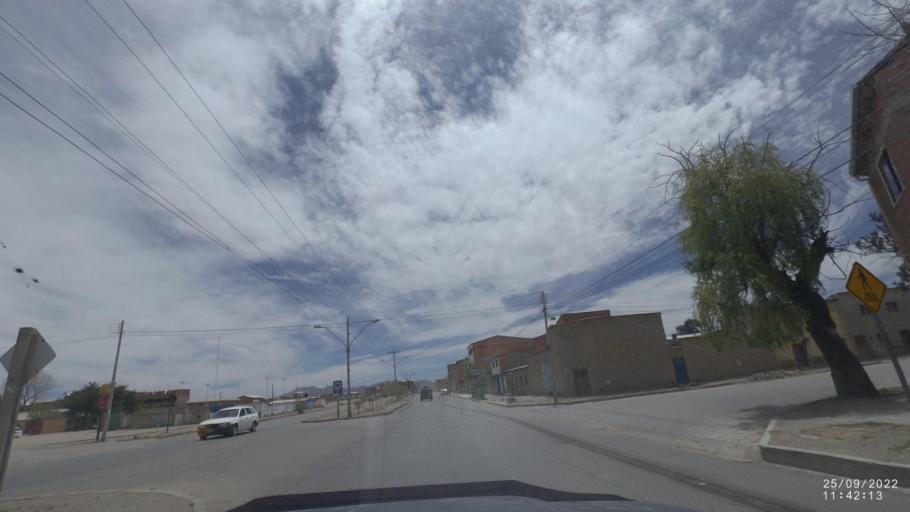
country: BO
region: Oruro
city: Challapata
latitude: -18.8990
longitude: -66.7766
